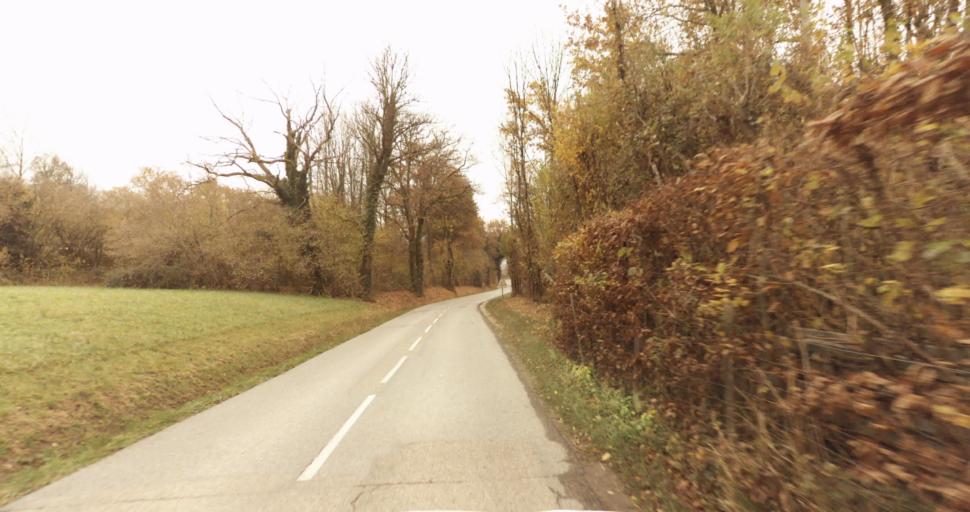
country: FR
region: Rhone-Alpes
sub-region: Departement de la Haute-Savoie
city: Saint-Felix
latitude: 45.7944
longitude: 5.9699
